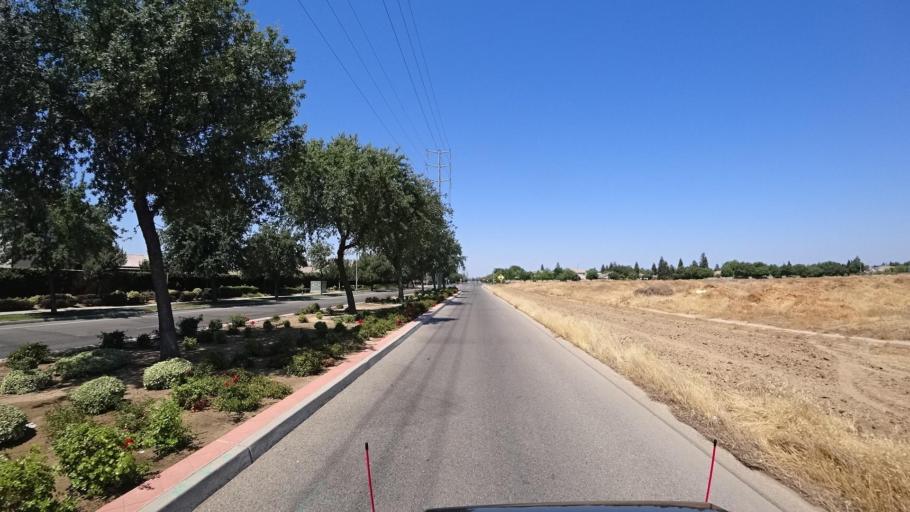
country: US
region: California
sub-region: Fresno County
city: Sunnyside
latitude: 36.7149
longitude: -119.6890
